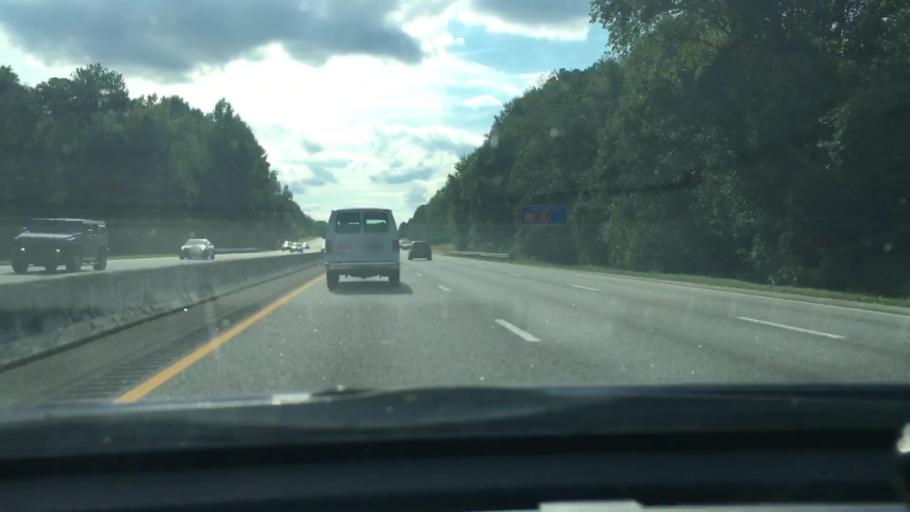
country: US
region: South Carolina
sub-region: Richland County
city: Dentsville
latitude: 34.0708
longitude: -81.0132
